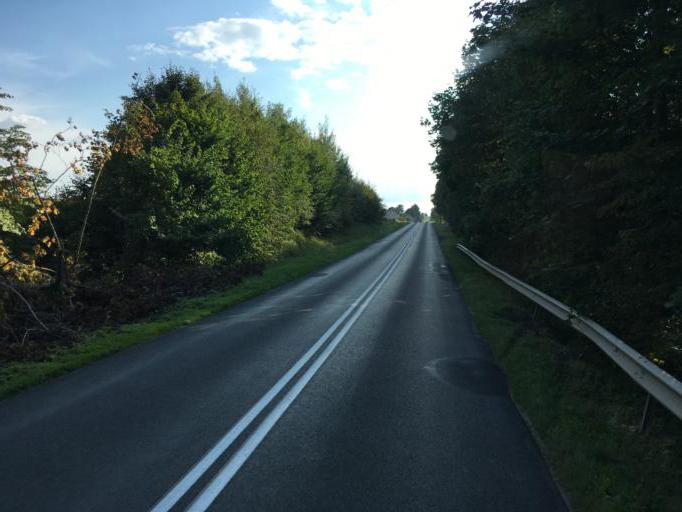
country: PL
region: Kujawsko-Pomorskie
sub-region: Powiat tucholski
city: Tuchola
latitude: 53.5452
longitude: 17.8608
